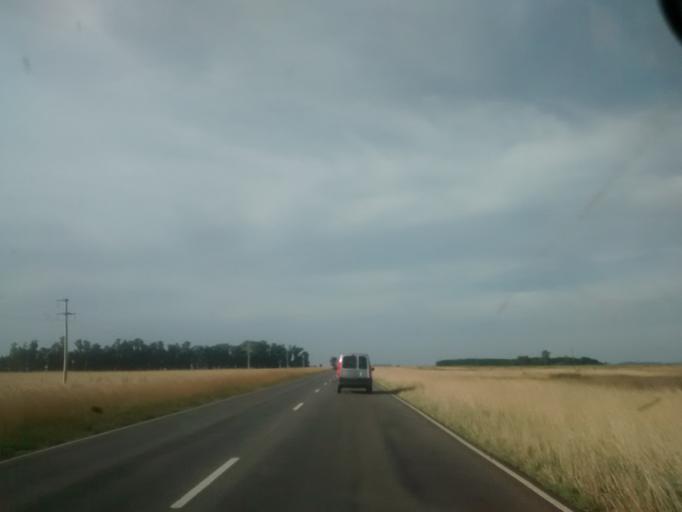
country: AR
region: Buenos Aires
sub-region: Partido de Ayacucho
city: Ayacucho
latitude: -36.9291
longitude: -58.5261
